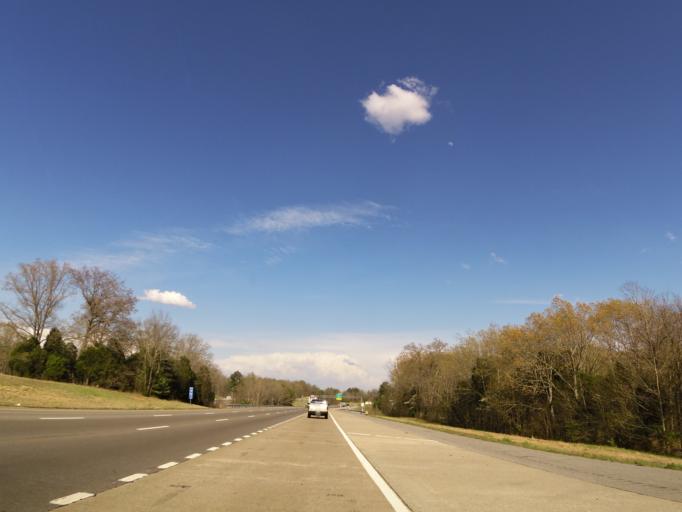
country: US
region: Tennessee
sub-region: Dickson County
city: Burns
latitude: 36.0242
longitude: -87.2851
